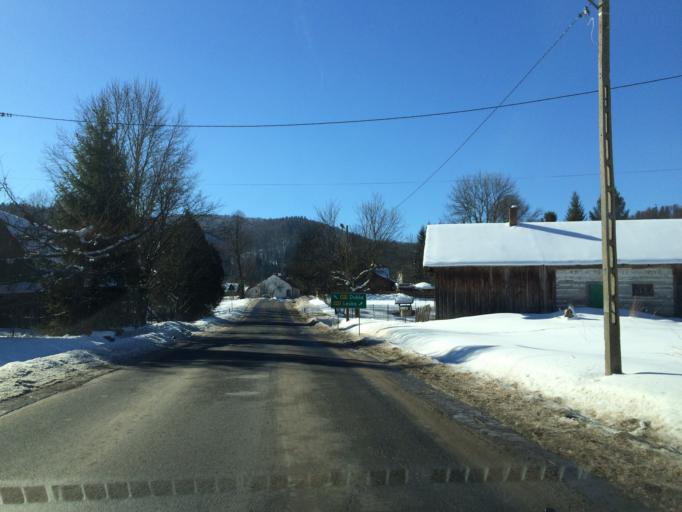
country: PL
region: Subcarpathian Voivodeship
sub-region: Powiat leski
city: Cisna
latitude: 49.2119
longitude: 22.3314
